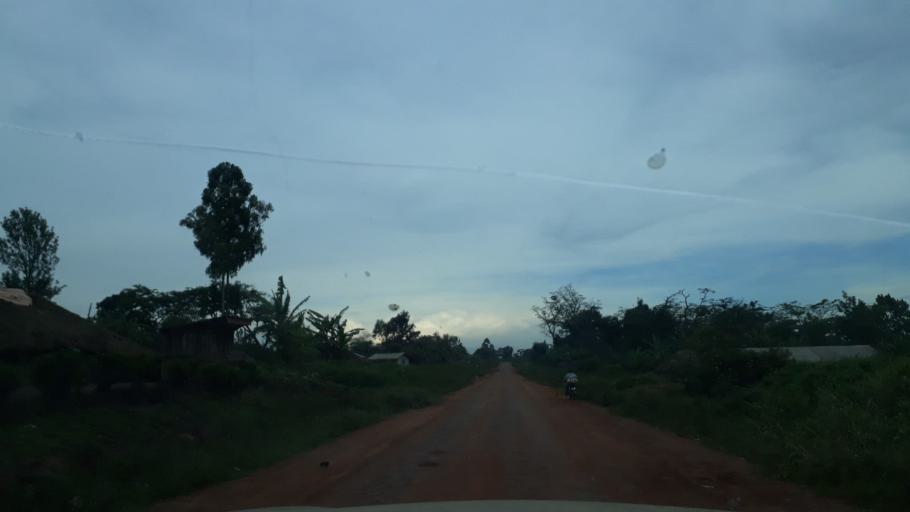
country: UG
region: Northern Region
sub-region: Zombo District
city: Paidha
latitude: 2.1774
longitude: 30.7107
